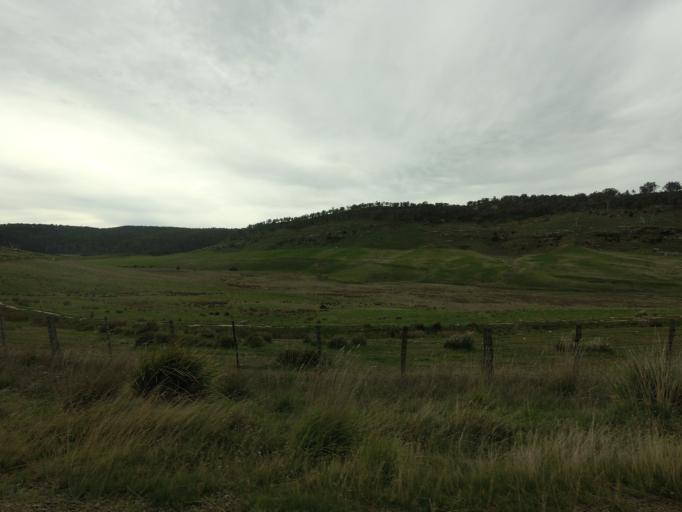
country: AU
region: Tasmania
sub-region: Derwent Valley
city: New Norfolk
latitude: -42.4014
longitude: 146.9196
